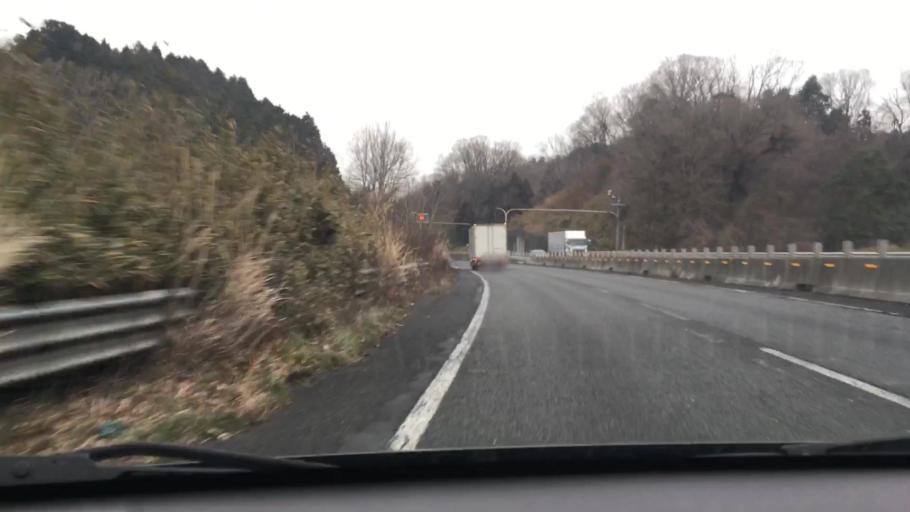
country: JP
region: Mie
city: Nabari
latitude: 34.6841
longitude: 136.0458
